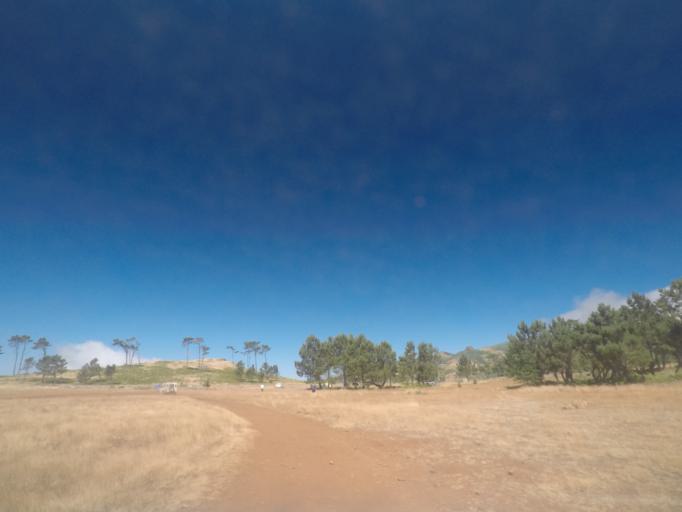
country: PT
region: Madeira
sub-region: Funchal
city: Nossa Senhora do Monte
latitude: 32.7117
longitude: -16.9106
